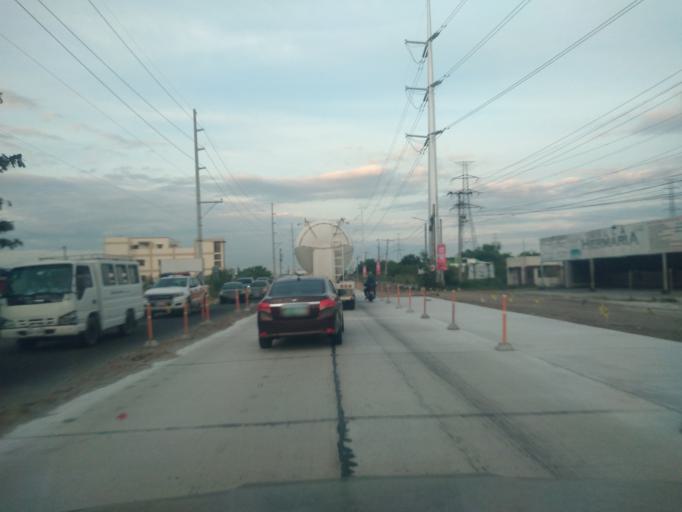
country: PH
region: Central Luzon
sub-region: Province of Pampanga
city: Bacolor
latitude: 14.9994
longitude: 120.6410
